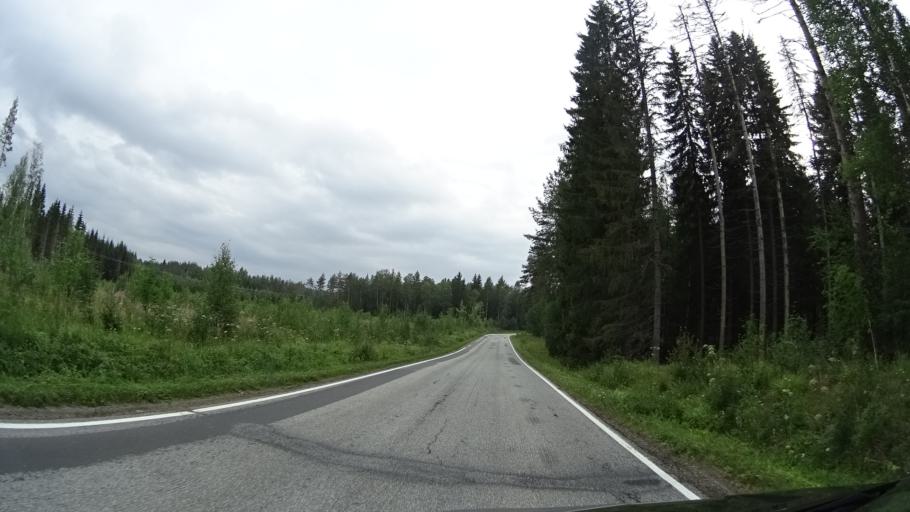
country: FI
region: Southern Savonia
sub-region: Savonlinna
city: Punkaharju
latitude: 61.7481
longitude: 29.5043
